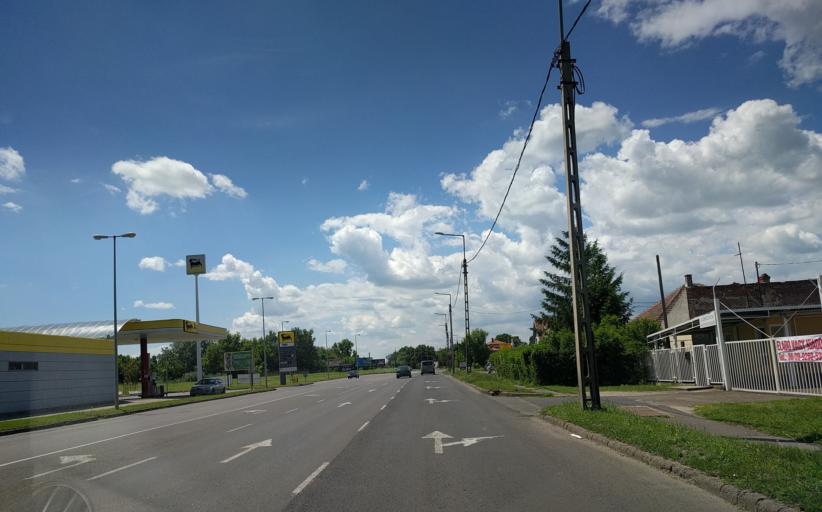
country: HU
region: Jasz-Nagykun-Szolnok
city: Szolnok
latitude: 47.1535
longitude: 20.1689
